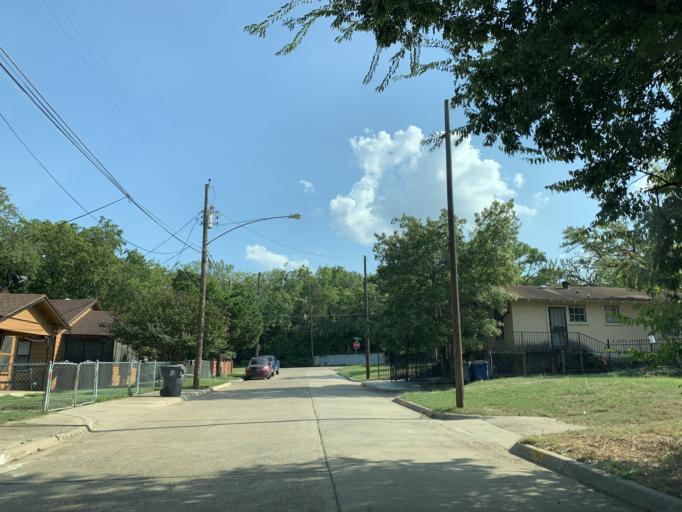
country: US
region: Texas
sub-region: Dallas County
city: Dallas
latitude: 32.7520
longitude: -96.8023
